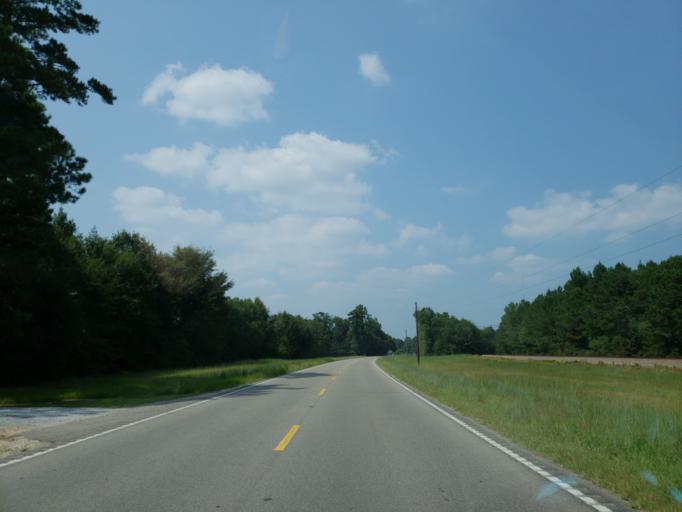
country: US
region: Mississippi
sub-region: Forrest County
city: Glendale
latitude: 31.4422
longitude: -89.2862
